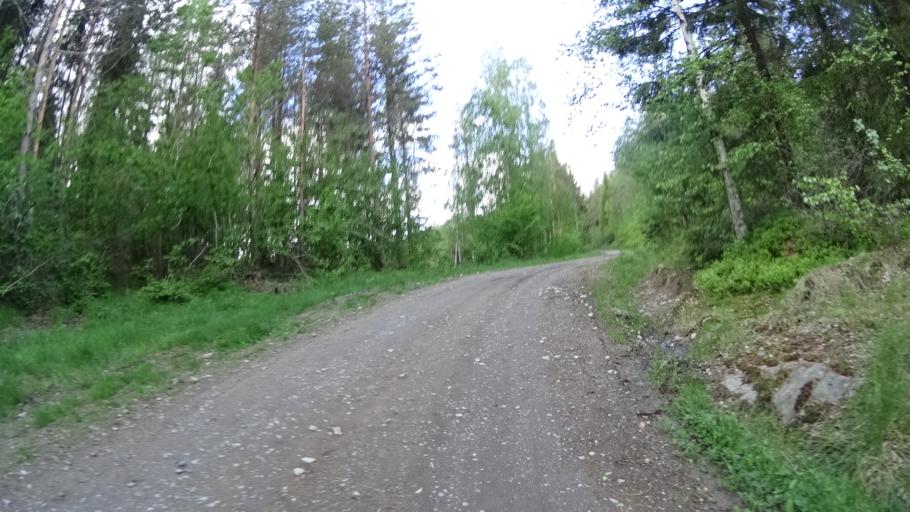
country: FI
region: Uusimaa
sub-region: Raaseporin
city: Karis
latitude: 60.1529
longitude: 23.6226
